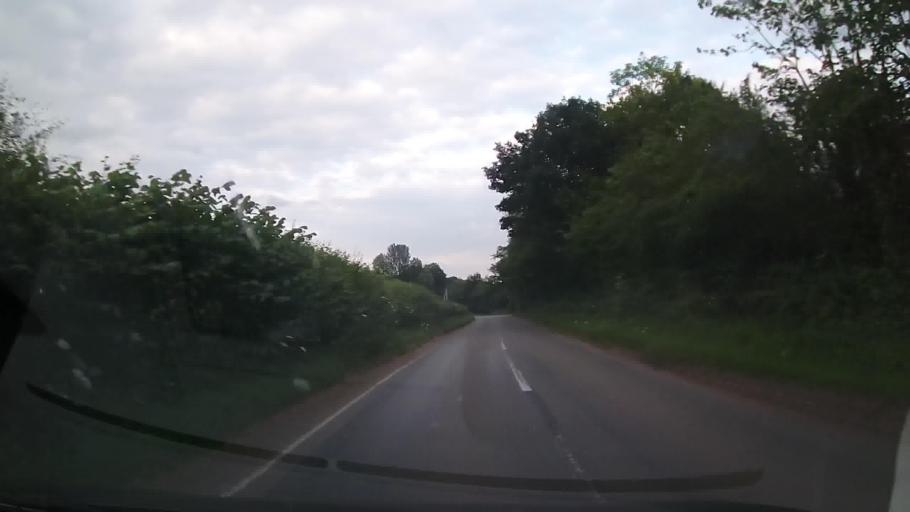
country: GB
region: Wales
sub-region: Sir Powys
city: Llanfechain
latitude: 52.8087
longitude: -3.1536
